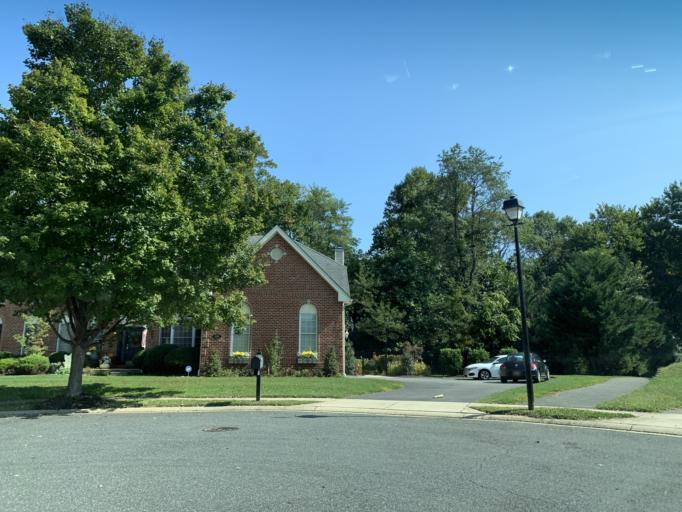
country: US
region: Maryland
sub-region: Harford County
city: Bel Air South
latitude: 39.4850
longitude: -76.3319
